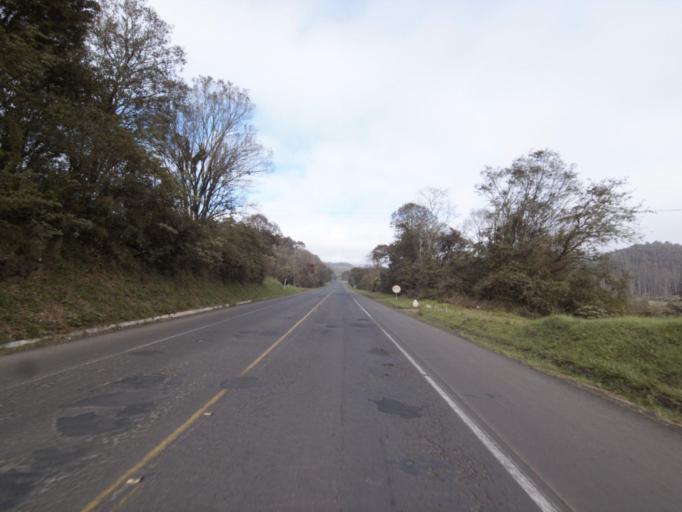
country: BR
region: Rio Grande do Sul
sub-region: Frederico Westphalen
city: Frederico Westphalen
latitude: -27.0252
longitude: -53.2320
